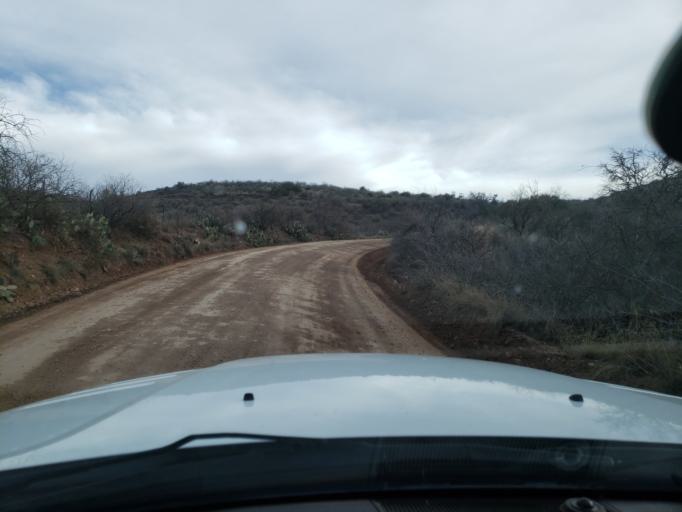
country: US
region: Arizona
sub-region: Pinal County
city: Oracle
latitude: 32.5511
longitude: -110.7080
